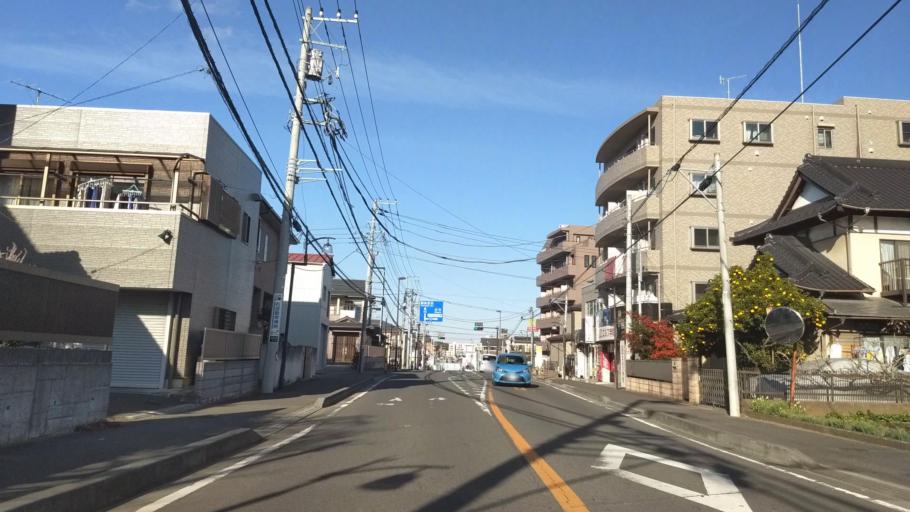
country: JP
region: Kanagawa
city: Isehara
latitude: 35.3774
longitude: 139.2770
